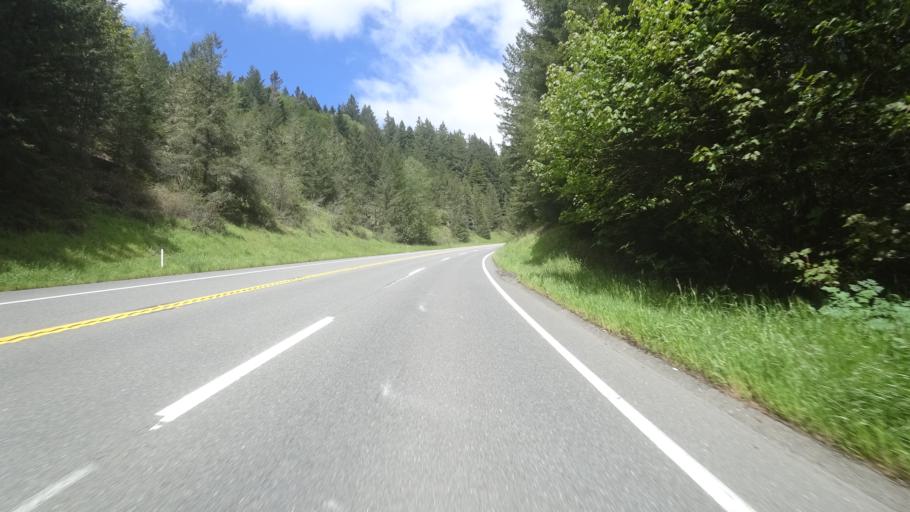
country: US
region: California
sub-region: Humboldt County
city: Blue Lake
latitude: 40.9279
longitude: -123.9117
